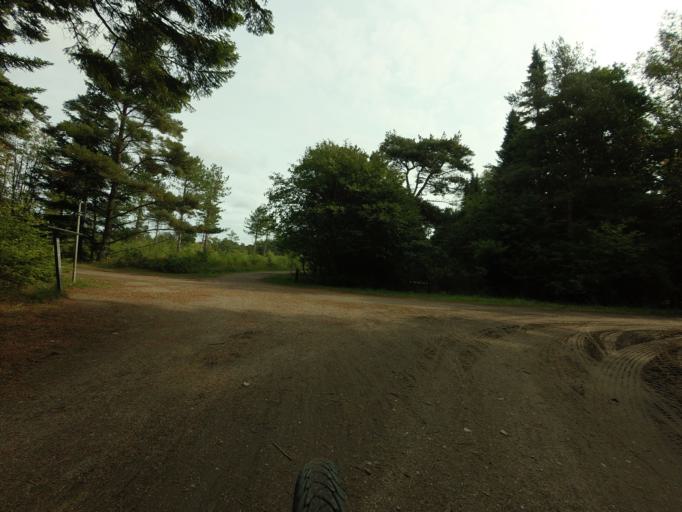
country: DK
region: North Denmark
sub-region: Hjorring Kommune
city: Sindal
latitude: 57.6097
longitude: 10.2761
